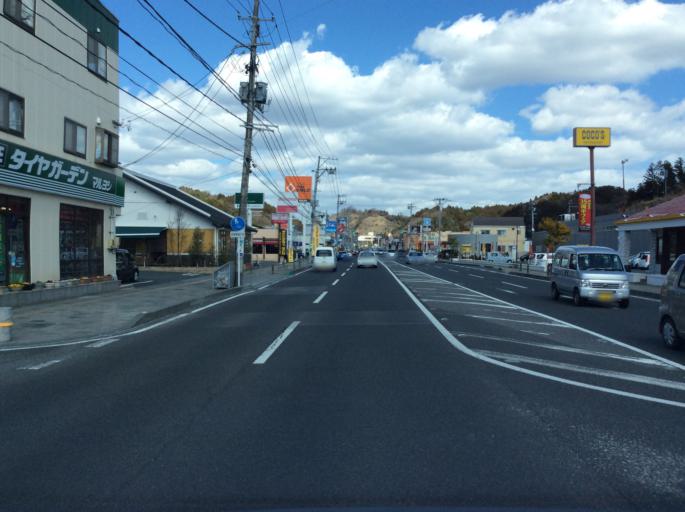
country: JP
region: Fukushima
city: Iwaki
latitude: 36.9634
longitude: 140.9044
